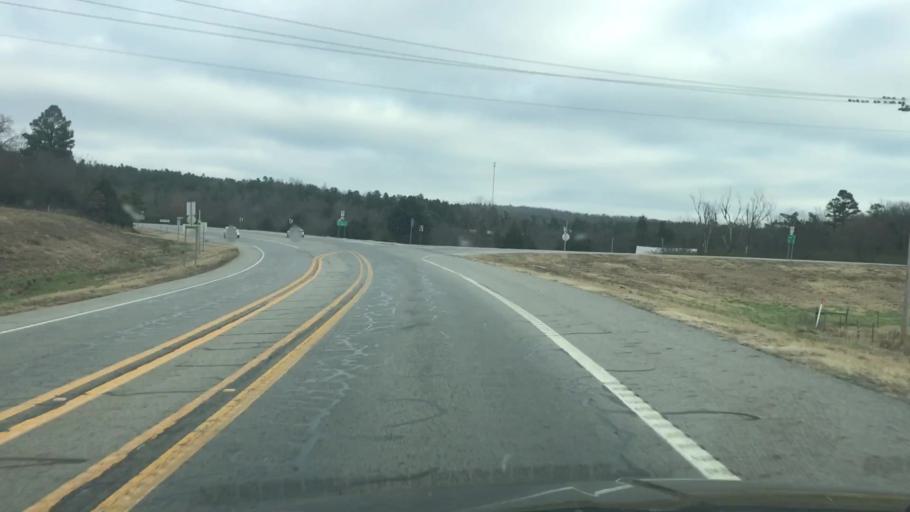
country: US
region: Arkansas
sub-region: Scott County
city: Waldron
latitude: 34.8078
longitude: -94.0395
